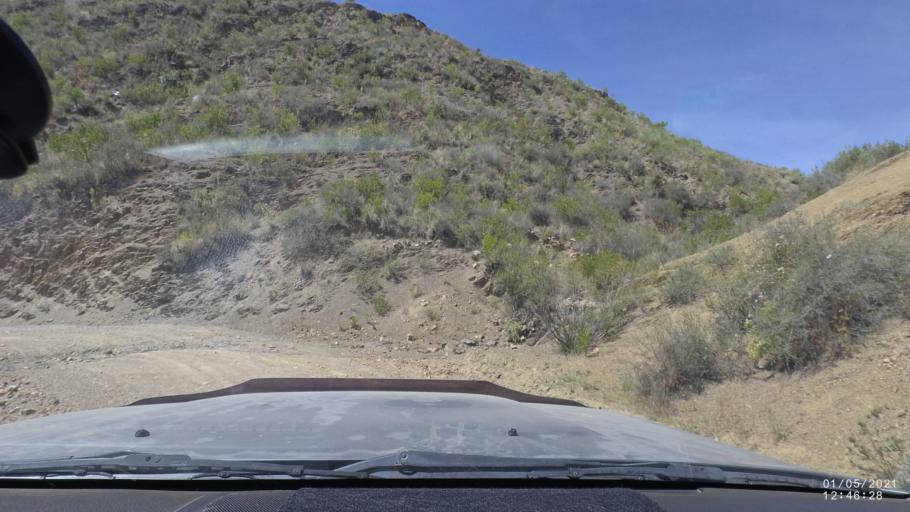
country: BO
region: Cochabamba
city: Capinota
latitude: -17.6877
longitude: -66.1601
